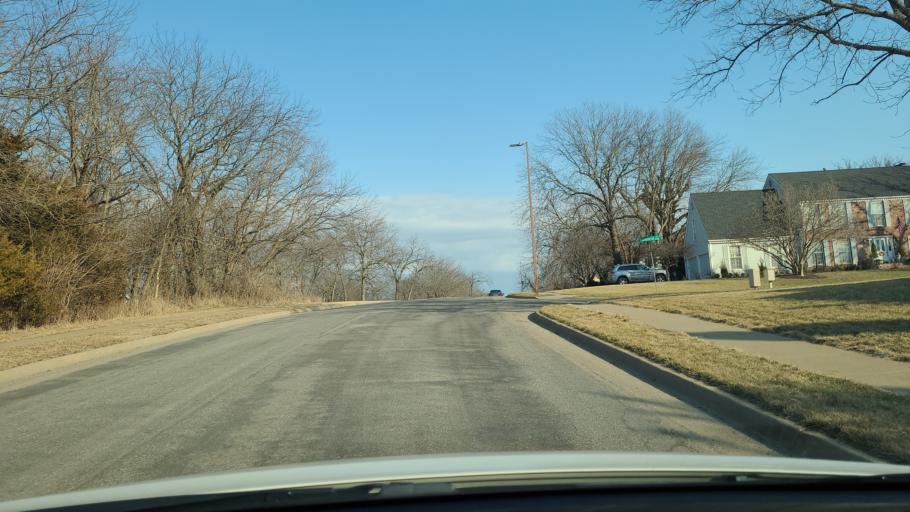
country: US
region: Kansas
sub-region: Douglas County
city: Lawrence
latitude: 38.9629
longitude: -95.3043
